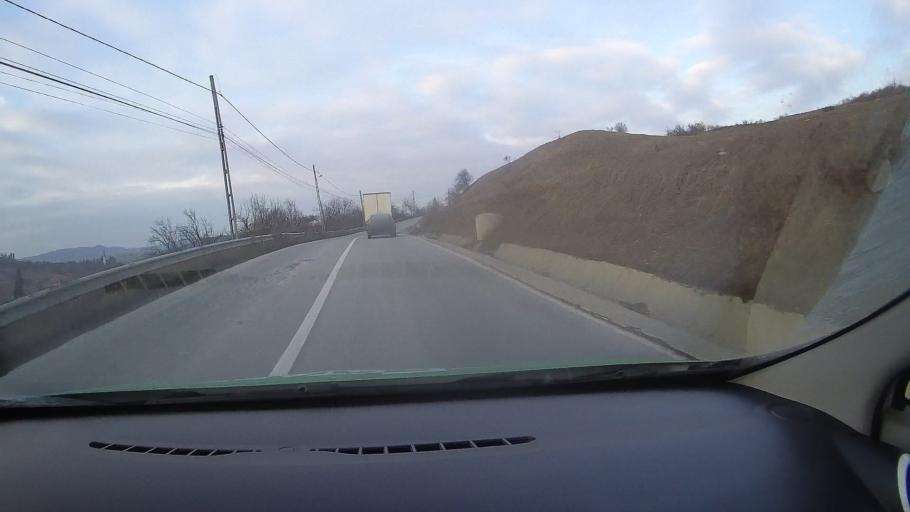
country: RO
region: Harghita
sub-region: Comuna Simonesti
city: Simonesti
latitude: 46.3294
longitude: 25.1040
